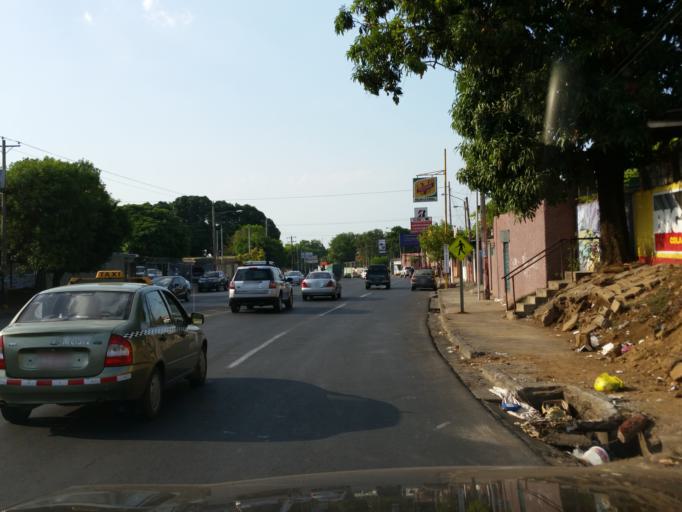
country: NI
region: Managua
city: Managua
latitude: 12.1279
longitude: -86.2562
